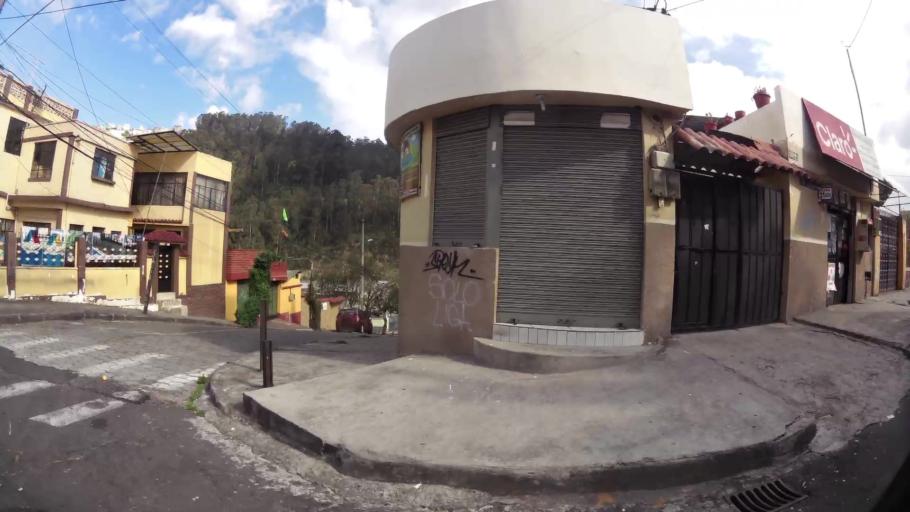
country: EC
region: Pichincha
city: Quito
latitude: -0.2303
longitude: -78.5031
